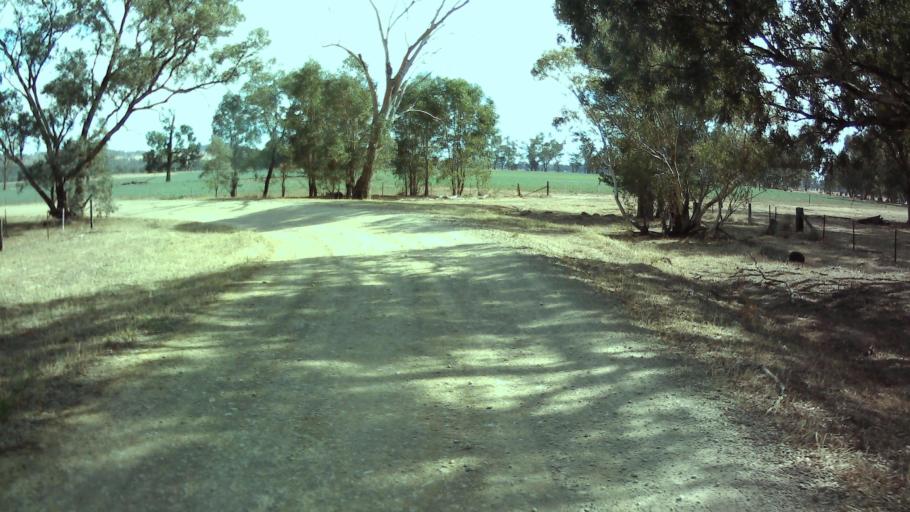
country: AU
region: New South Wales
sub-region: Weddin
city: Grenfell
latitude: -33.6874
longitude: 148.3053
